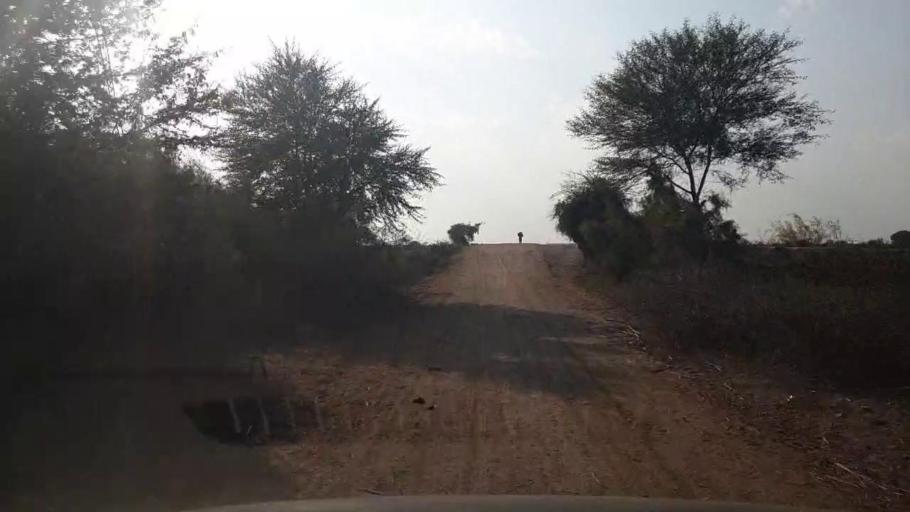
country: PK
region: Sindh
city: Hala
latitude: 25.8537
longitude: 68.3577
